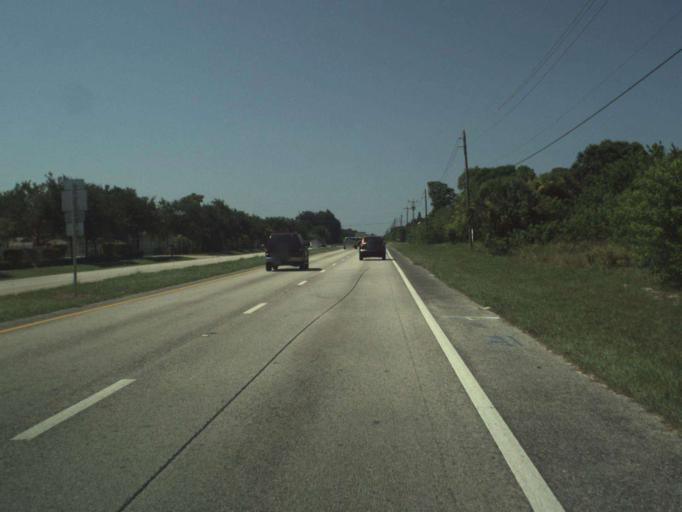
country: US
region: Florida
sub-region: Indian River County
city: Gifford
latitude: 27.6942
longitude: -80.4137
